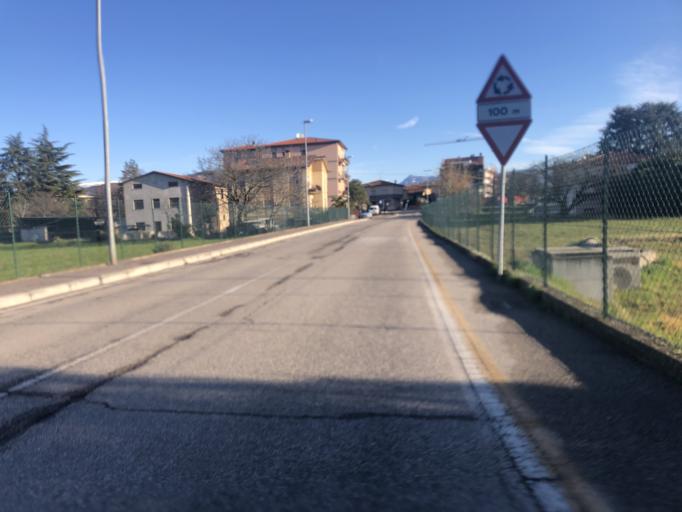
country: IT
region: Veneto
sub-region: Provincia di Verona
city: Pescantina
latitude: 45.4920
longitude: 10.8707
